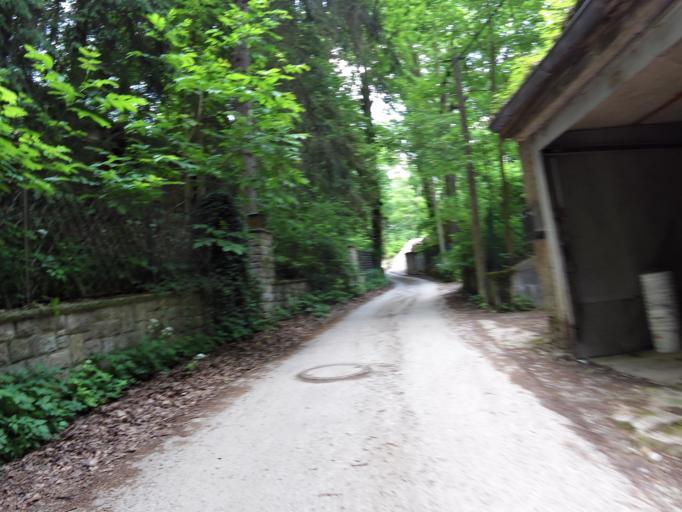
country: DE
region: Bavaria
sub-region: Regierungsbezirk Unterfranken
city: Wuerzburg
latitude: 49.7705
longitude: 9.8893
